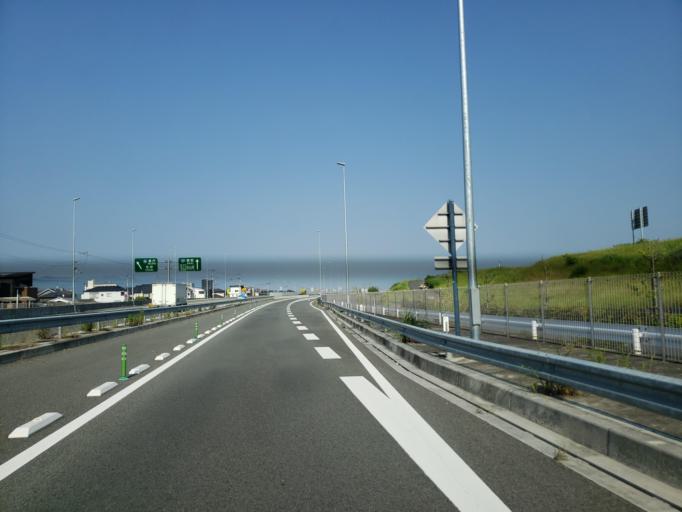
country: JP
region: Ehime
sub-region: Shikoku-chuo Shi
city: Matsuyama
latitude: 33.8068
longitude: 132.7488
